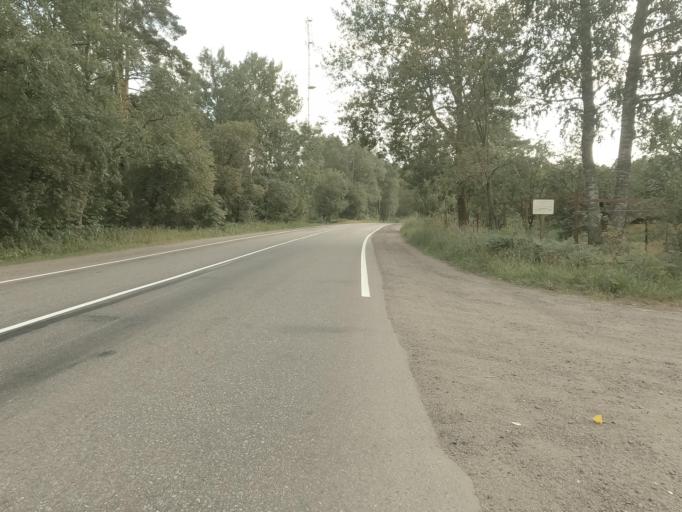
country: RU
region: Leningrad
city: Lesogorskiy
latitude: 60.8601
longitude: 28.9681
